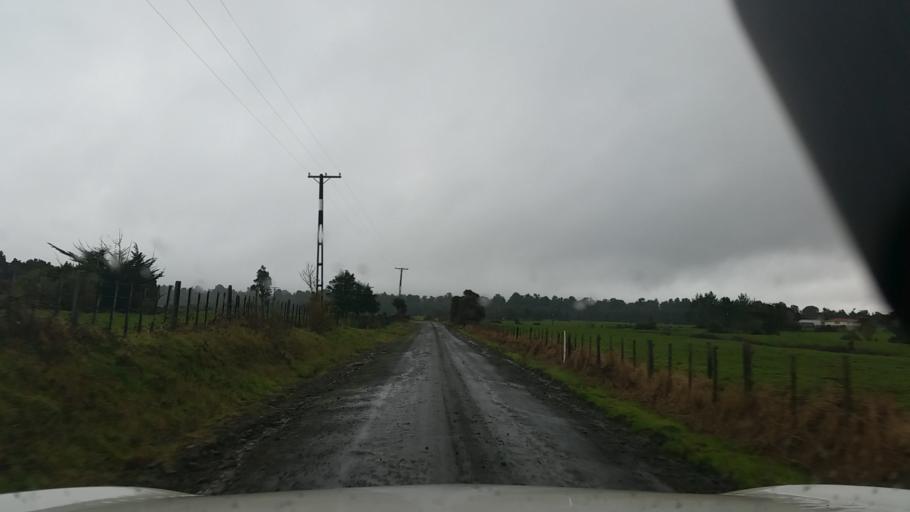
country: NZ
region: Taranaki
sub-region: South Taranaki District
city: Eltham
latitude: -39.2772
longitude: 174.1849
